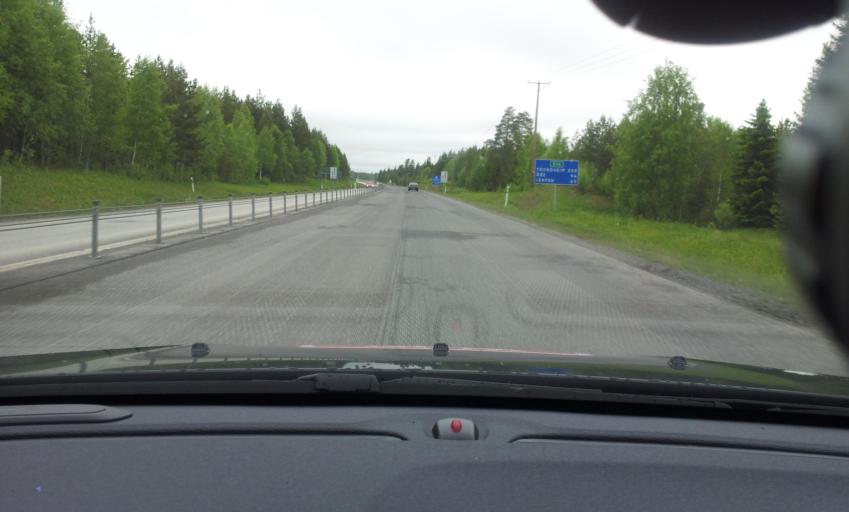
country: SE
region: Jaemtland
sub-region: OEstersunds Kommun
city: Ostersund
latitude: 63.2215
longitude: 14.6271
